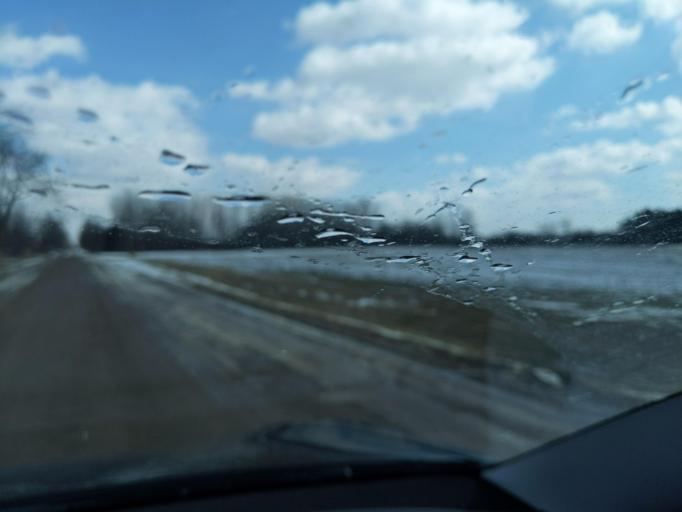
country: US
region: Michigan
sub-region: Livingston County
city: Fowlerville
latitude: 42.6140
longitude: -84.1126
